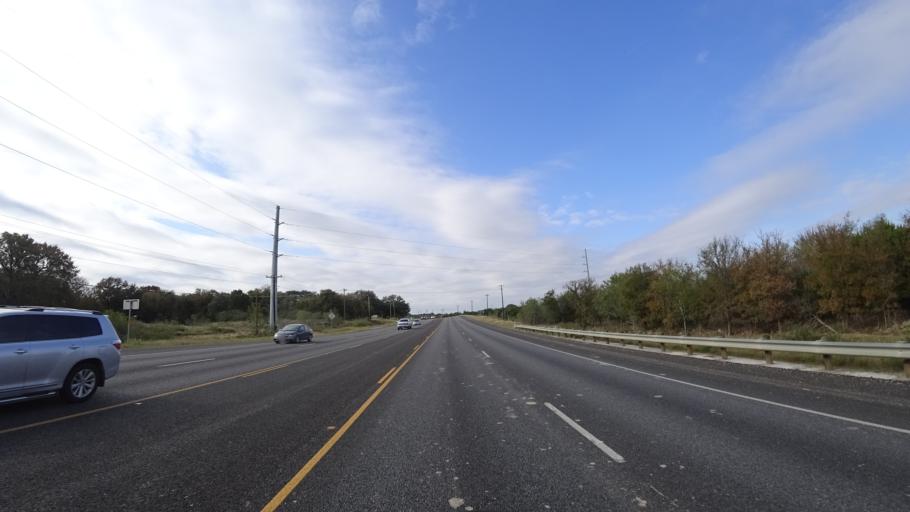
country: US
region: Texas
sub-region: Travis County
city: Manchaca
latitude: 30.1333
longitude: -97.8547
